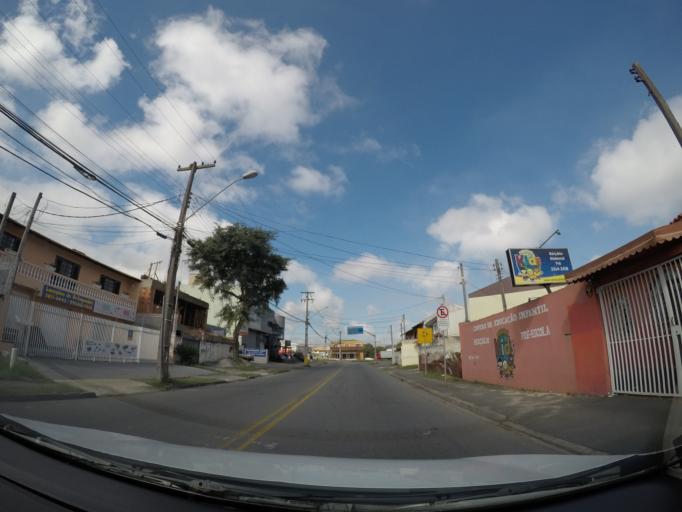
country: BR
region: Parana
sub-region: Sao Jose Dos Pinhais
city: Sao Jose dos Pinhais
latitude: -25.4960
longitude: -49.2163
